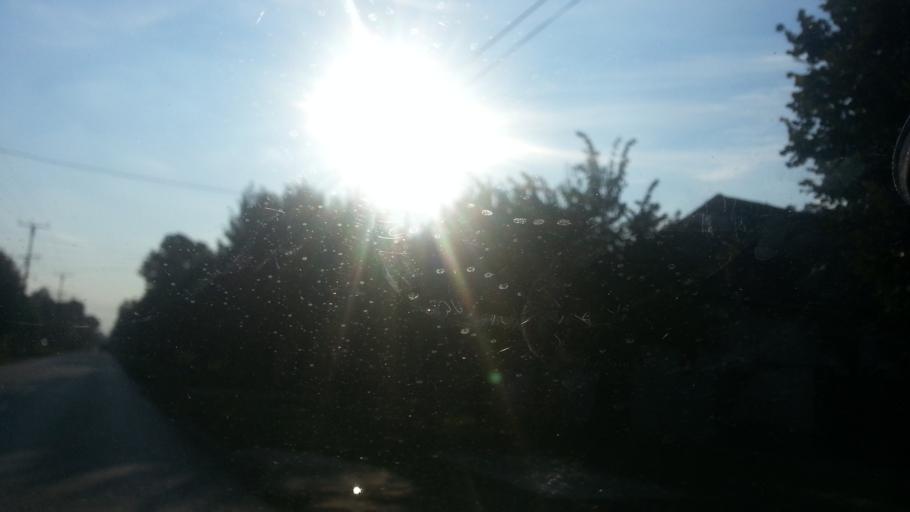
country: RS
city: Novi Slankamen
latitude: 45.1321
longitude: 20.2472
